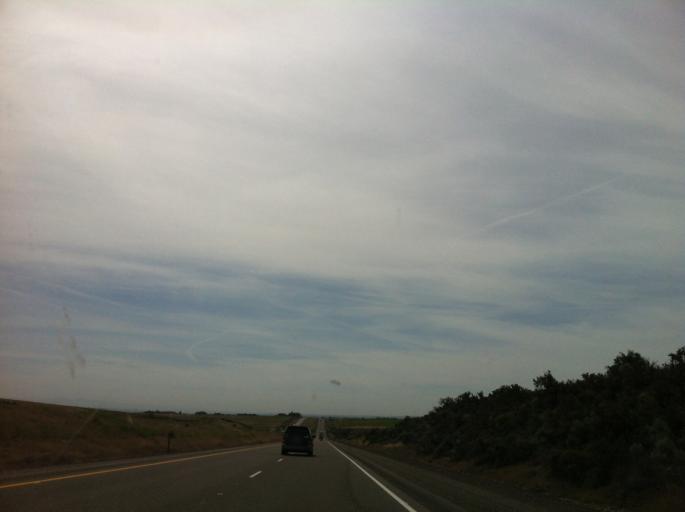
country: US
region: Oregon
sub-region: Malheur County
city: Ontario
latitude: 44.1032
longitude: -117.0446
